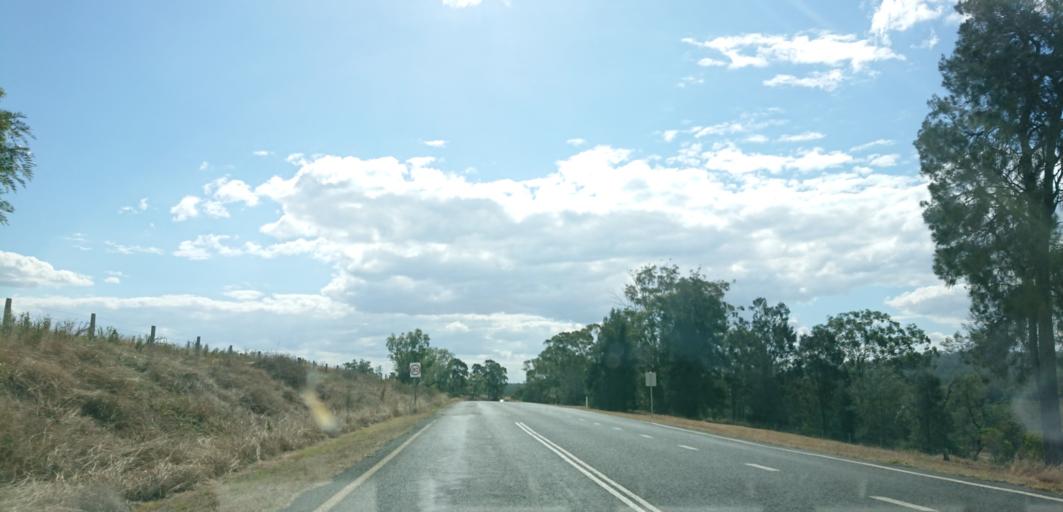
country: AU
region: Queensland
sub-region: Toowoomba
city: Top Camp
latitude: -27.7884
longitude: 152.0998
